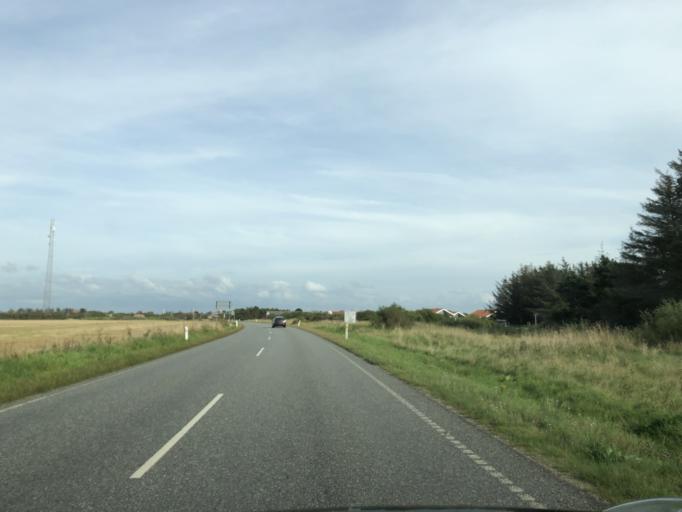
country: DK
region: Central Jutland
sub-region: Holstebro Kommune
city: Ulfborg
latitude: 56.3193
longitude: 8.1394
